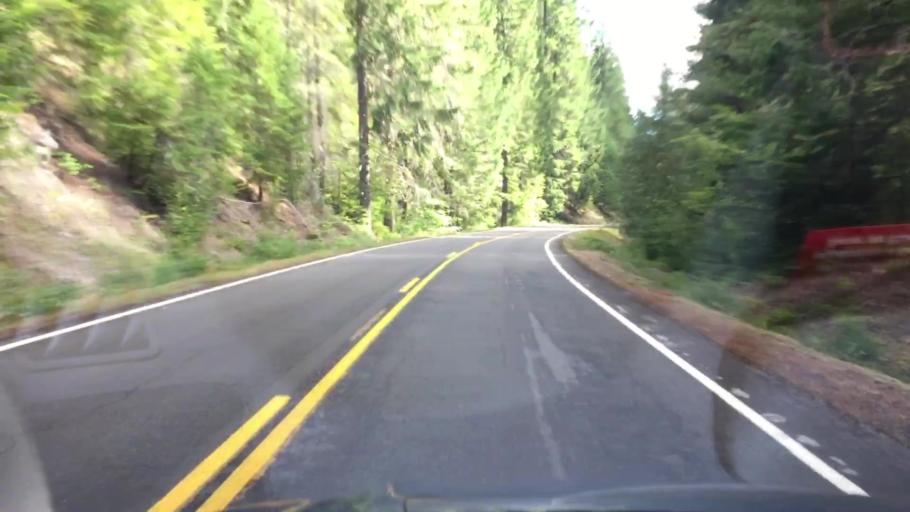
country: US
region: Washington
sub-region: Pierce County
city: Buckley
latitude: 46.7471
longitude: -121.6195
